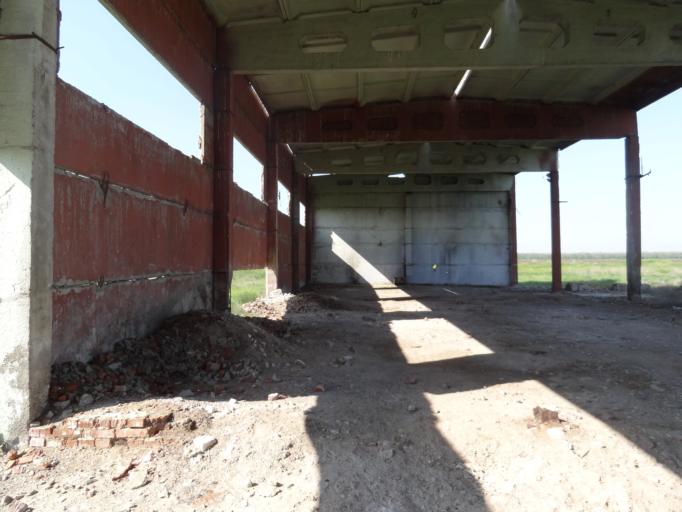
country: RU
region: Saratov
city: Engel's
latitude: 51.4254
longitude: 46.1210
